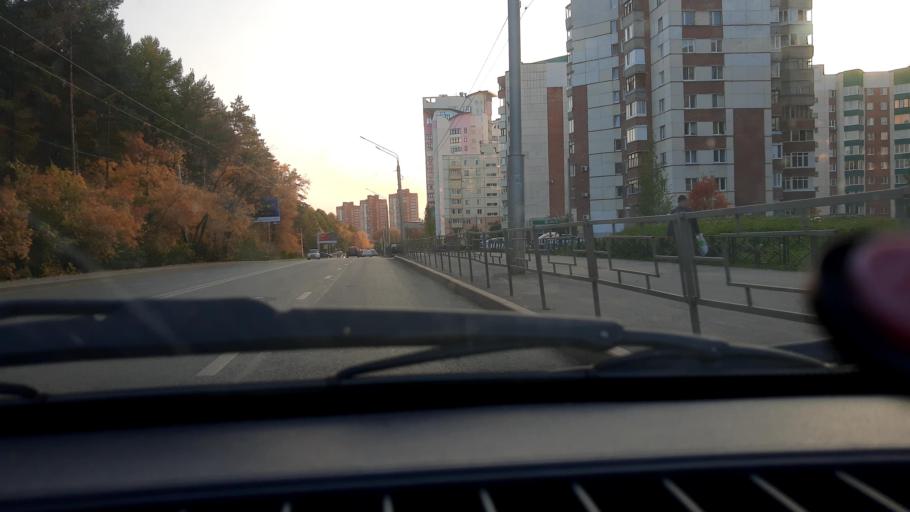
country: RU
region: Bashkortostan
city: Ufa
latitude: 54.6958
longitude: 56.0059
